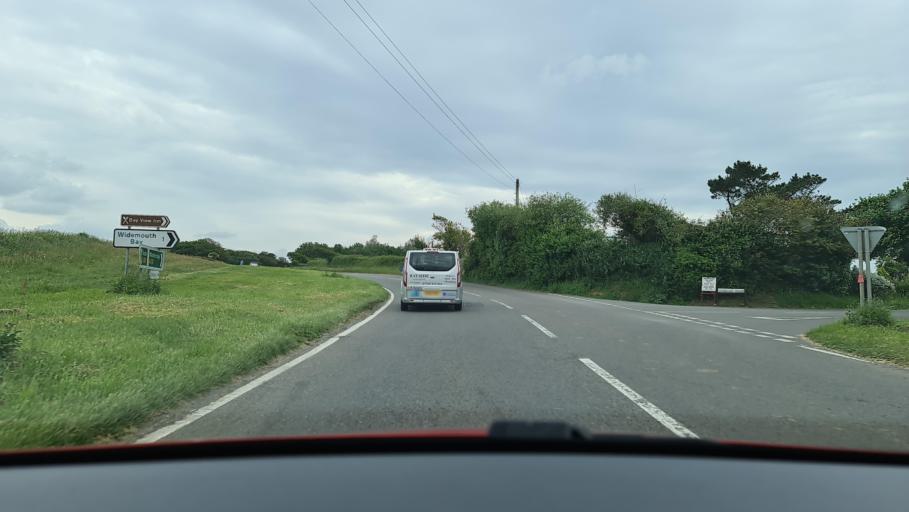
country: GB
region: England
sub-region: Cornwall
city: Poundstock
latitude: 50.7861
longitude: -4.5345
